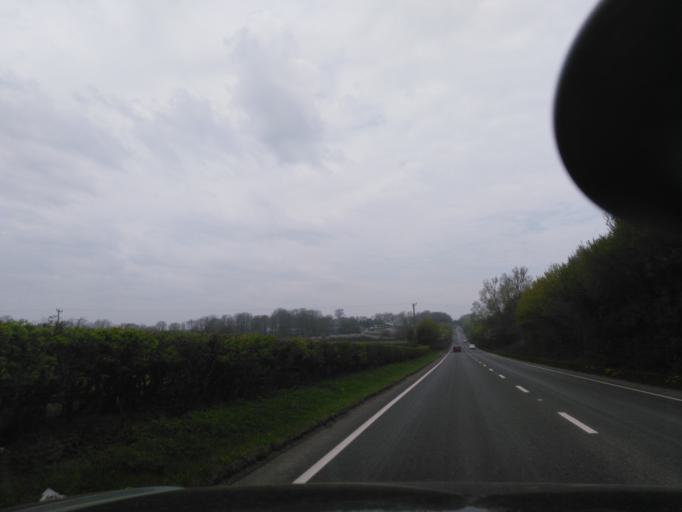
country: GB
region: England
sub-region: Somerset
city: Frome
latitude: 51.2087
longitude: -2.3290
